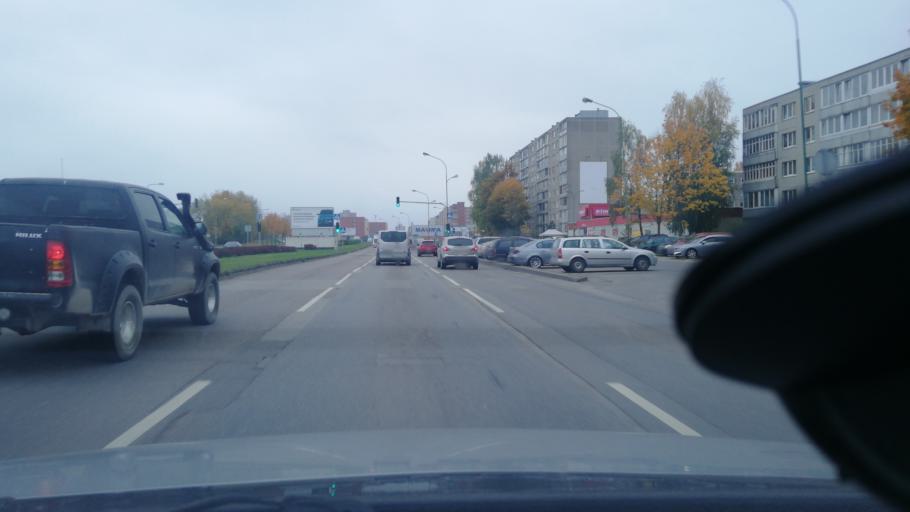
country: LT
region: Klaipedos apskritis
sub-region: Klaipeda
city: Klaipeda
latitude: 55.6803
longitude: 21.1869
